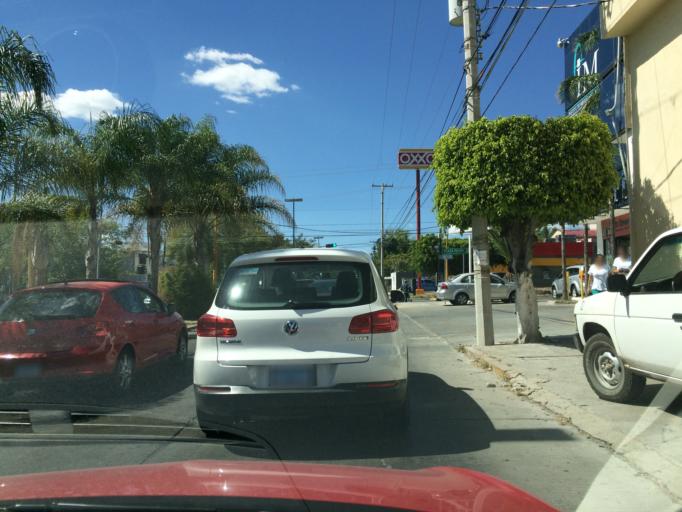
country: MX
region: Guanajuato
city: Leon
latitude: 21.1192
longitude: -101.6981
